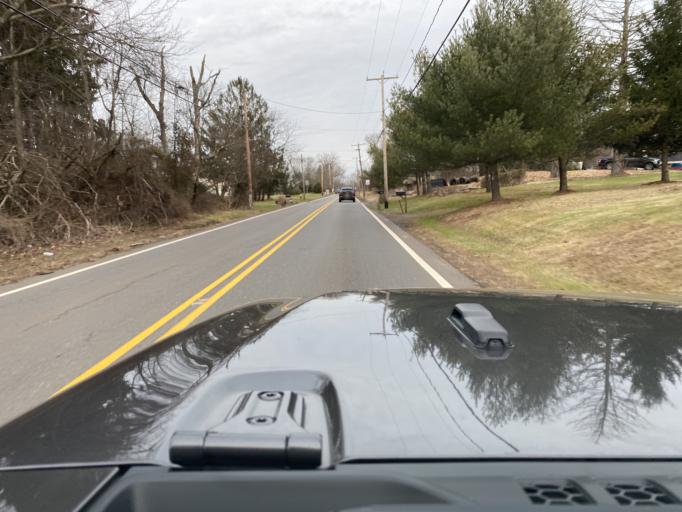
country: US
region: New Jersey
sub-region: Somerset County
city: Bloomingdale
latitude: 40.5004
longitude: -74.7110
